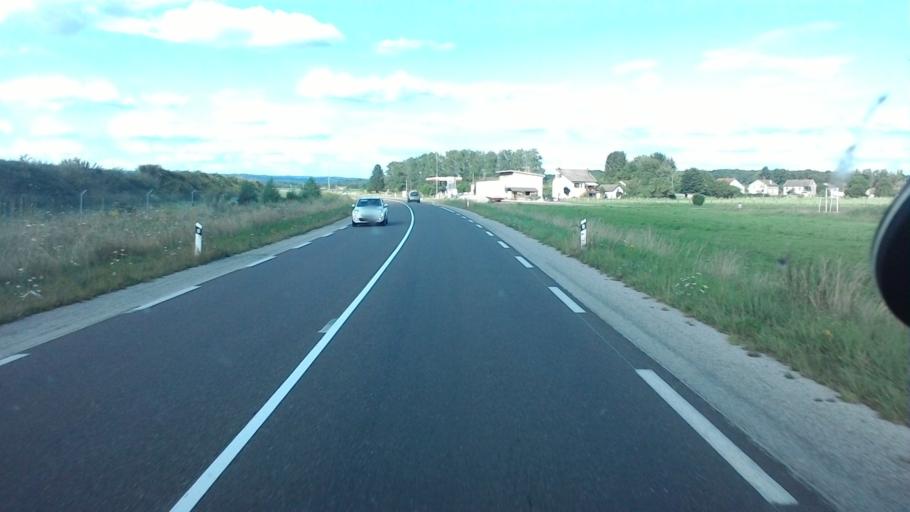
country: FR
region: Franche-Comte
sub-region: Departement de la Haute-Saone
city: Saint-Sauveur
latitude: 47.7737
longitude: 6.3628
